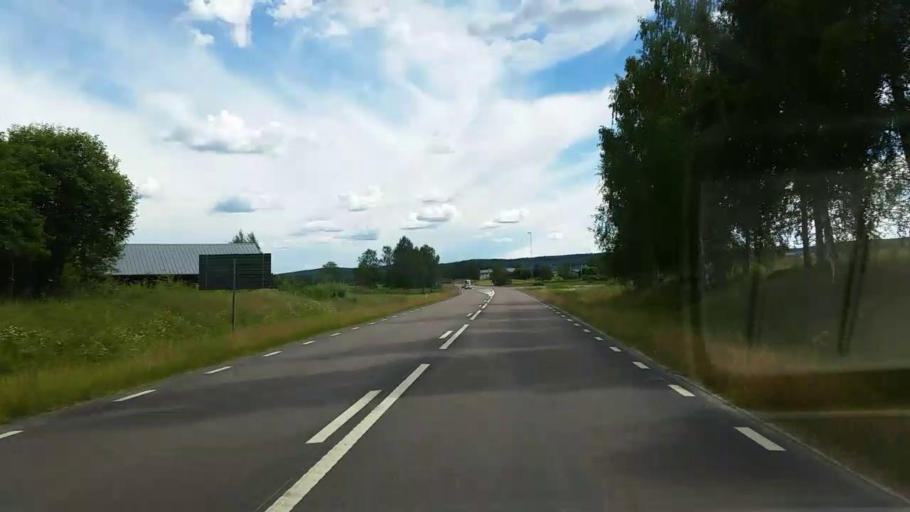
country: SE
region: Gaevleborg
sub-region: Ovanakers Kommun
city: Edsbyn
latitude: 61.3786
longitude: 15.8370
